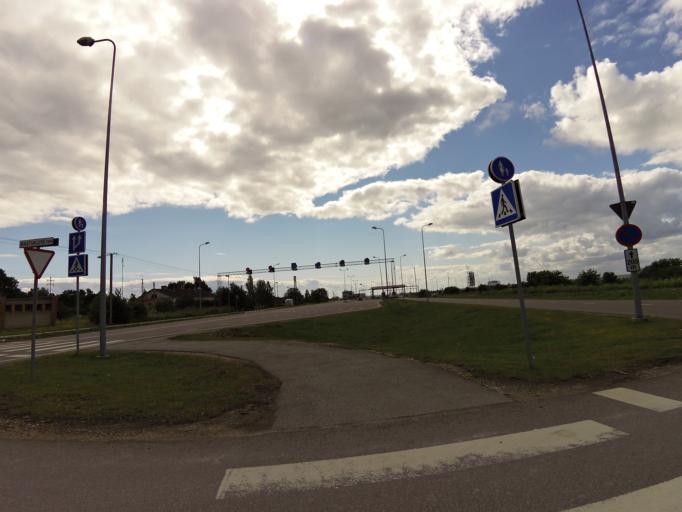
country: EE
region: Laeaene
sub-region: Haapsalu linn
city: Haapsalu
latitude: 58.9087
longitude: 23.4293
